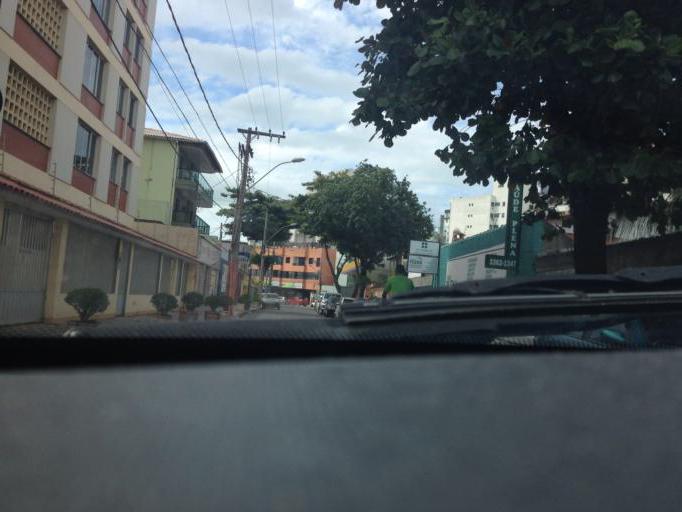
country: BR
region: Espirito Santo
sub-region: Guarapari
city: Guarapari
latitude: -20.6721
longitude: -40.5019
